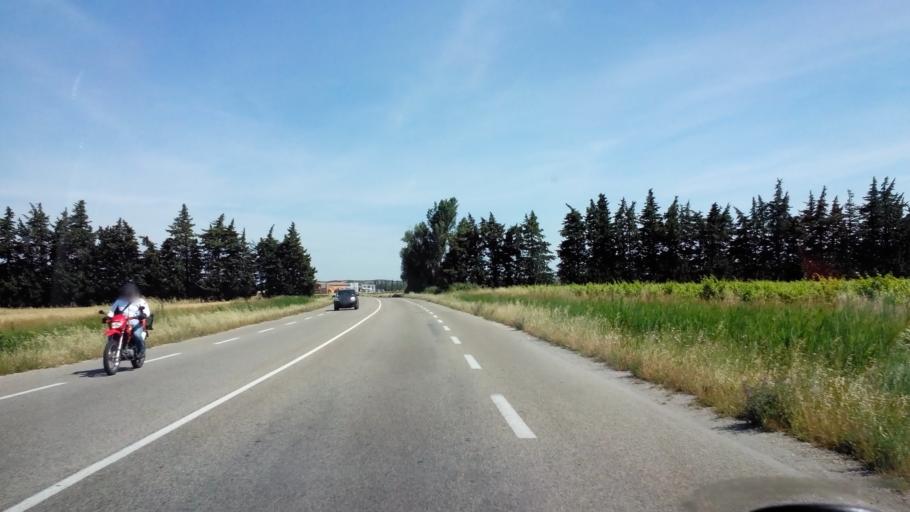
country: FR
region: Languedoc-Roussillon
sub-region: Departement du Gard
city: Les Angles
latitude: 43.9831
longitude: 4.7492
